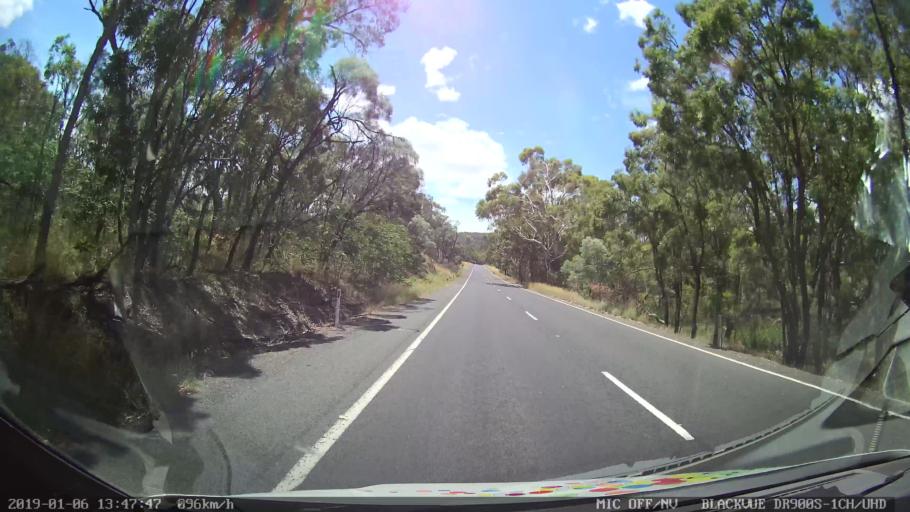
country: AU
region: New South Wales
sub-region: Tamworth Municipality
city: Kootingal
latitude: -30.9600
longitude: 151.1064
